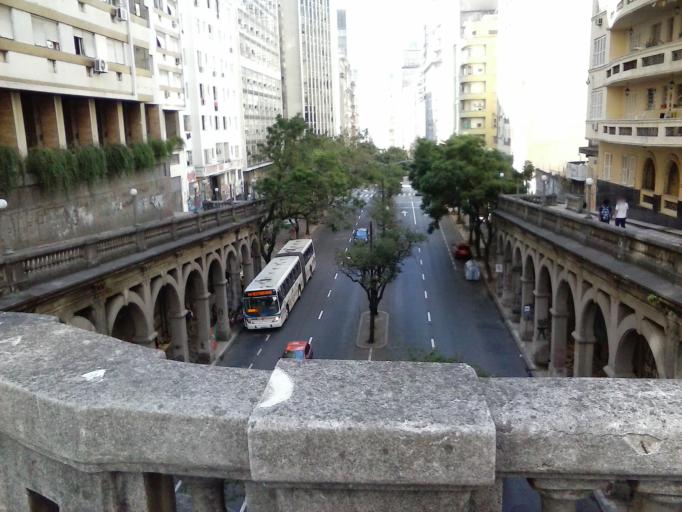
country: BR
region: Rio Grande do Sul
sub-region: Porto Alegre
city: Porto Alegre
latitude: -30.0336
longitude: -51.2279
